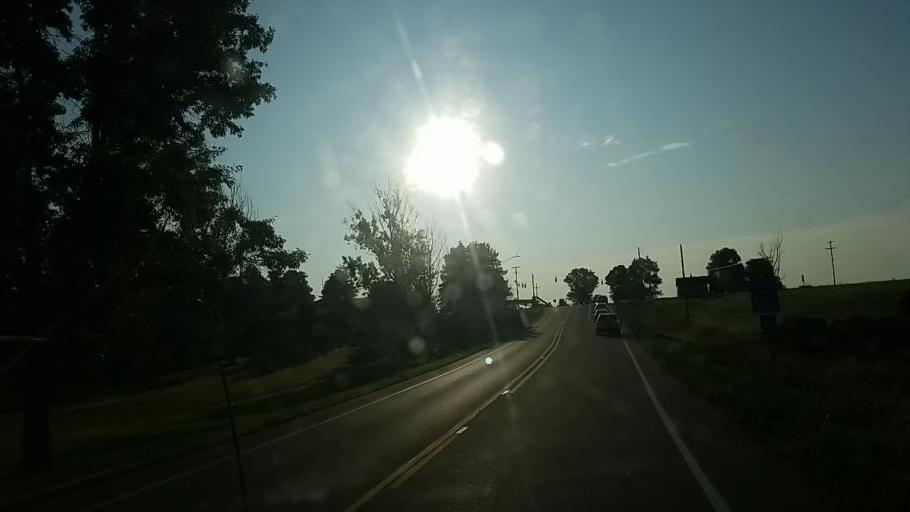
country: US
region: Michigan
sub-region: Montcalm County
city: Greenville
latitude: 43.2501
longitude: -85.2544
